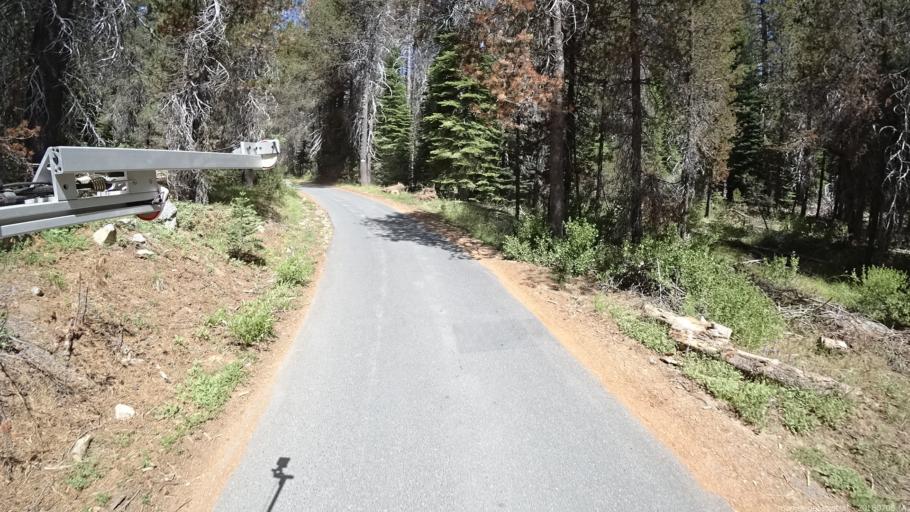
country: US
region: California
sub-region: Madera County
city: Oakhurst
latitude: 37.4464
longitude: -119.4717
